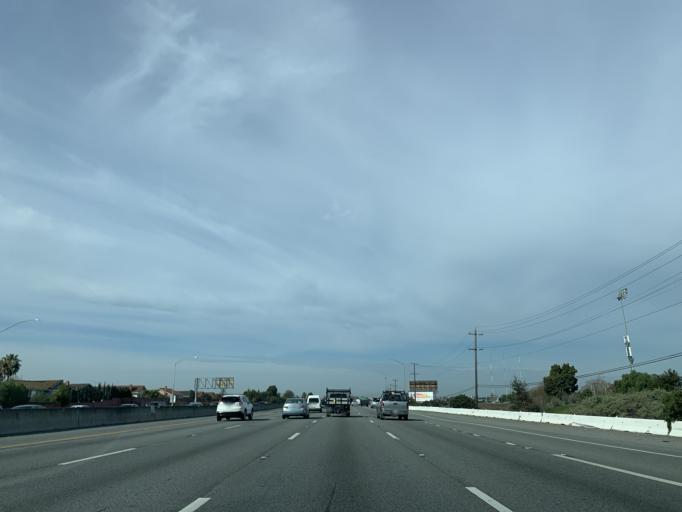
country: US
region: California
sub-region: San Mateo County
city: Belmont
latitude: 37.5291
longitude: -122.2724
